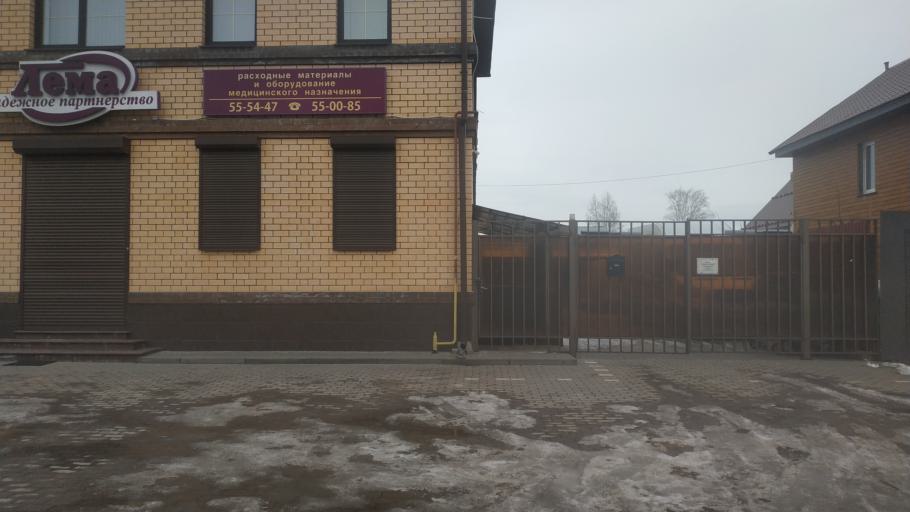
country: RU
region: Tverskaya
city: Tver
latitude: 56.8911
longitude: 35.8526
